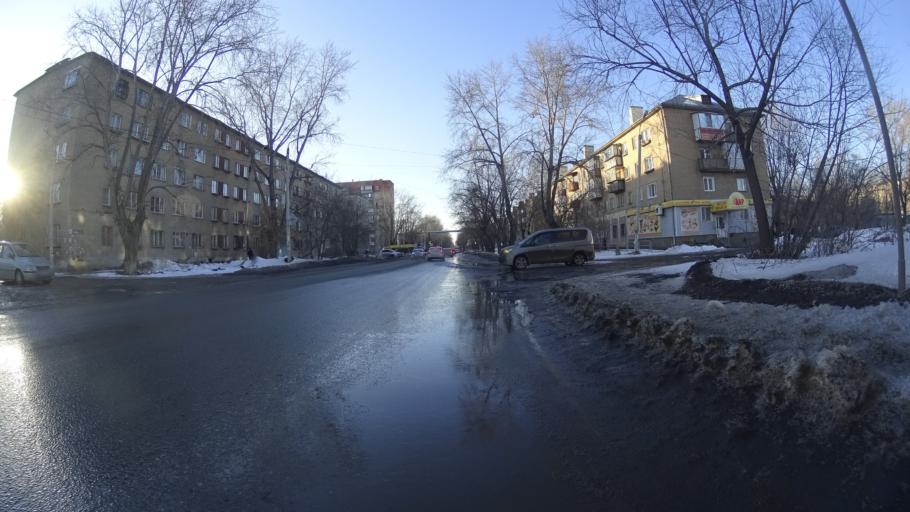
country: RU
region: Chelyabinsk
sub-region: Gorod Chelyabinsk
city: Chelyabinsk
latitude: 55.1263
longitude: 61.4731
